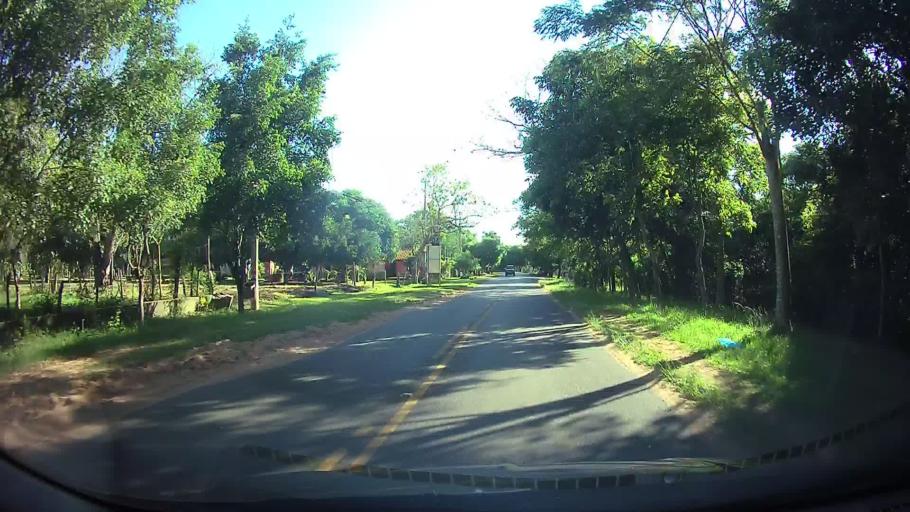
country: PY
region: Cordillera
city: Atyra
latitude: -25.2936
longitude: -57.1834
